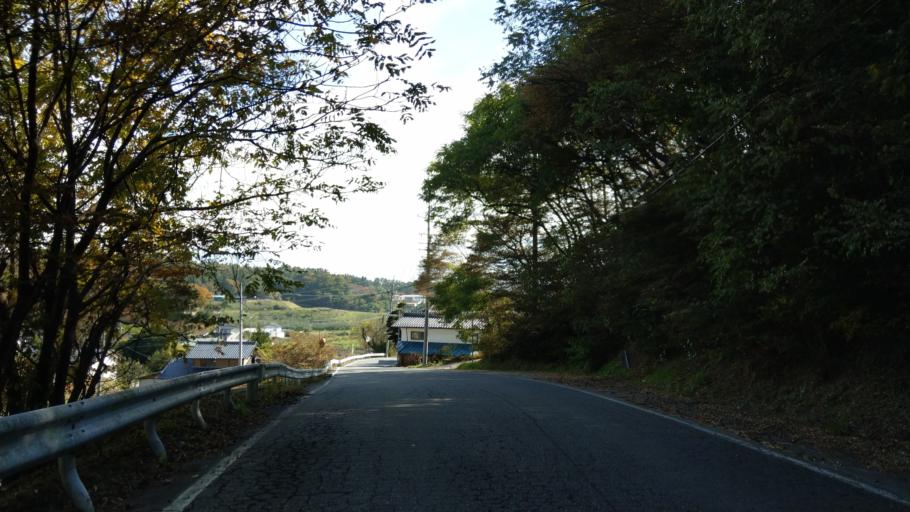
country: JP
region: Nagano
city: Komoro
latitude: 36.3399
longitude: 138.4424
